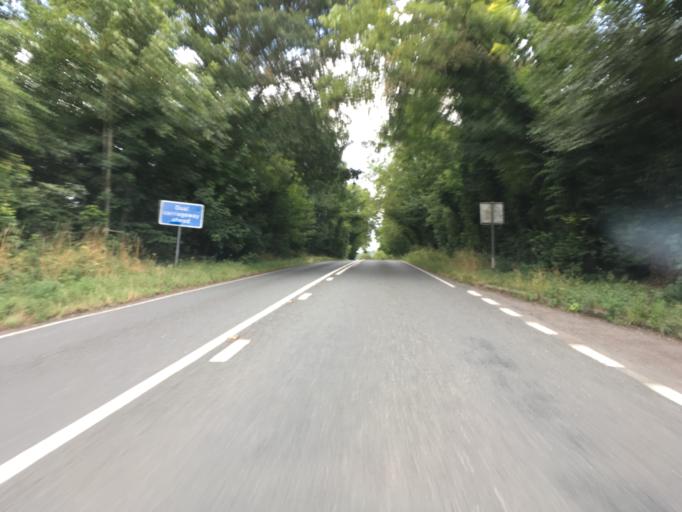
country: GB
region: England
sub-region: Hampshire
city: Kings Worthy
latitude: 51.1166
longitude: -1.2721
